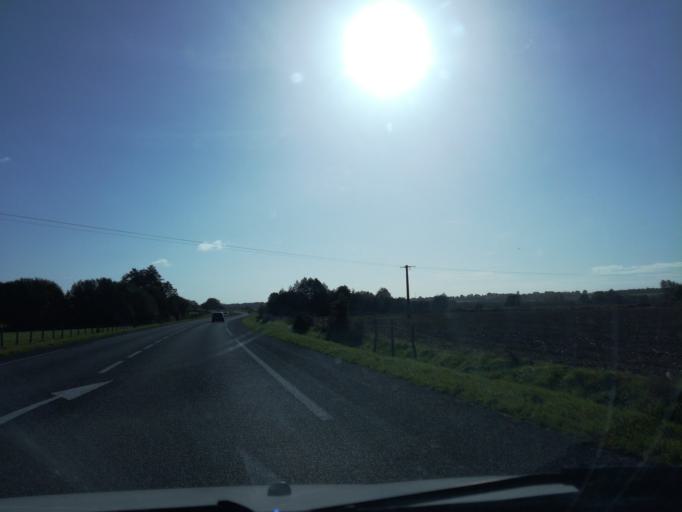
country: FR
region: Pays de la Loire
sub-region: Departement de Maine-et-Loire
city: Pouance
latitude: 47.7654
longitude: -1.2151
